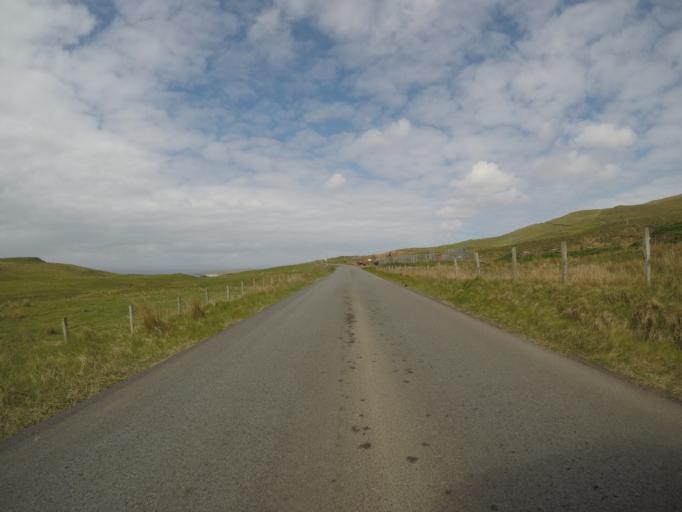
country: GB
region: Scotland
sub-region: Highland
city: Portree
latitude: 57.5983
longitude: -6.3758
